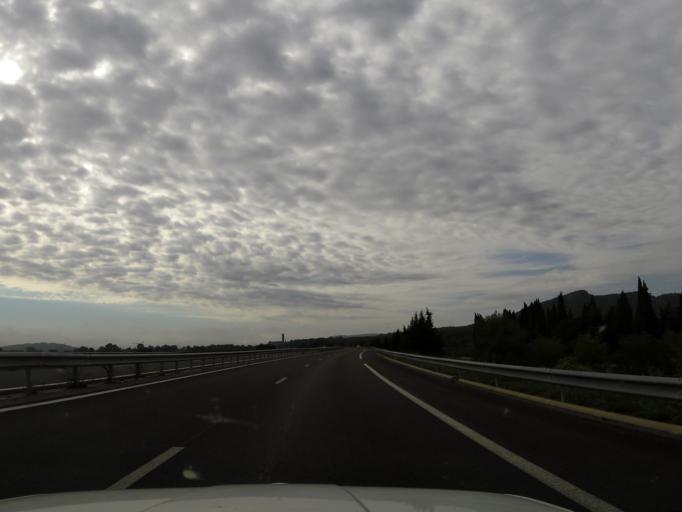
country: FR
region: Languedoc-Roussillon
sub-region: Departement du Gard
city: Vezenobres
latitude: 44.0086
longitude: 4.1741
